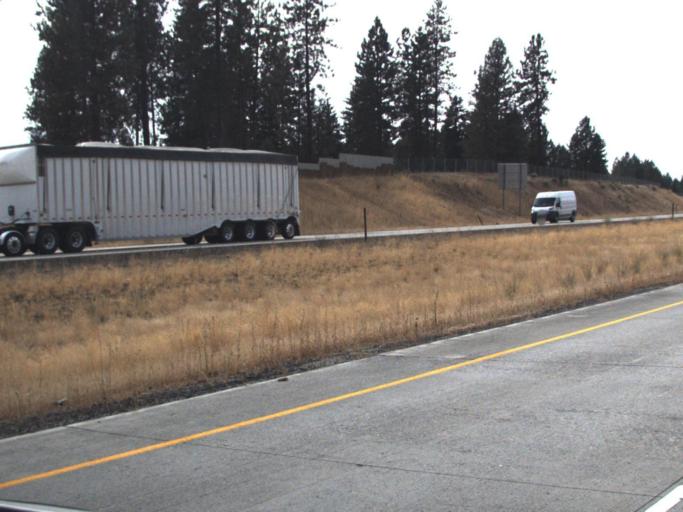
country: US
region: Washington
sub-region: Spokane County
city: Mead
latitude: 47.7789
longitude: -117.3816
